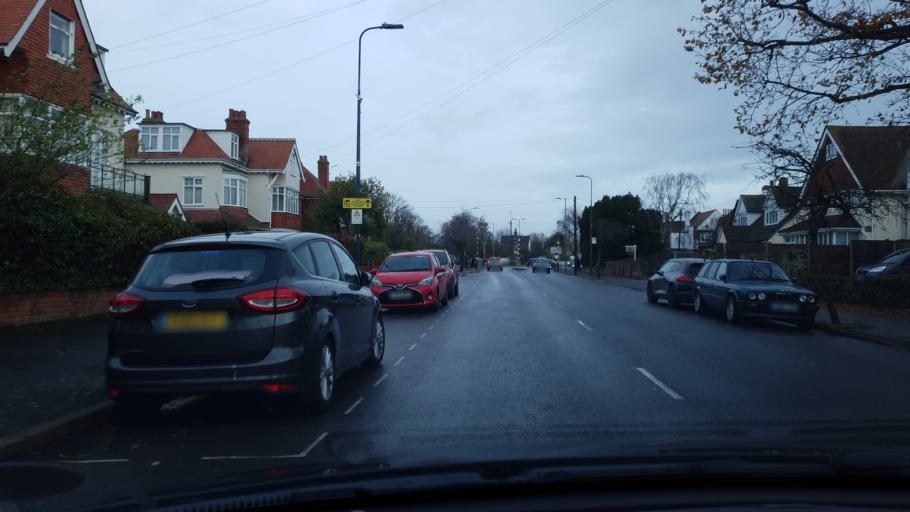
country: GB
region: England
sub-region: Essex
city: Frinton-on-Sea
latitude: 51.8361
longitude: 1.2446
